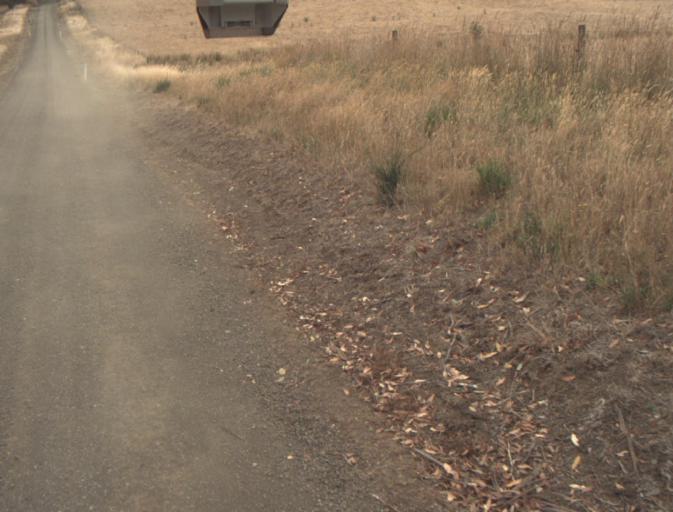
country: AU
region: Tasmania
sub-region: Northern Midlands
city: Evandale
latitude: -41.4617
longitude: 147.4542
